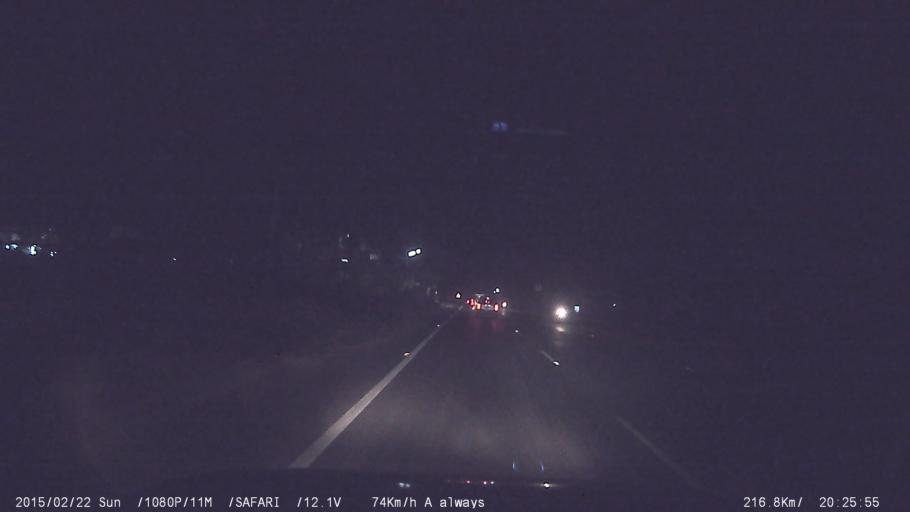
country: IN
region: Tamil Nadu
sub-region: Dindigul
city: Dindigul
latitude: 10.3185
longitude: 77.9053
